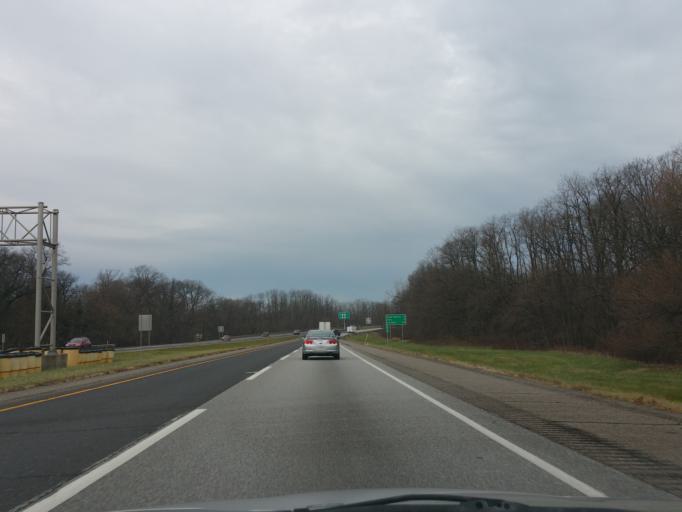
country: US
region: Indiana
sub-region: Porter County
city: Portage
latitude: 41.5812
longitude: -87.1928
